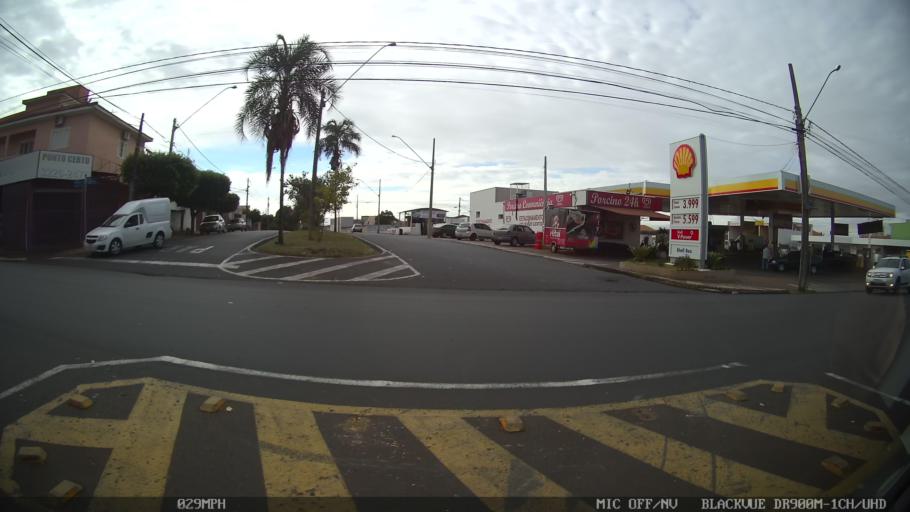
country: BR
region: Sao Paulo
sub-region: Sao Jose Do Rio Preto
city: Sao Jose do Rio Preto
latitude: -20.8328
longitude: -49.3717
